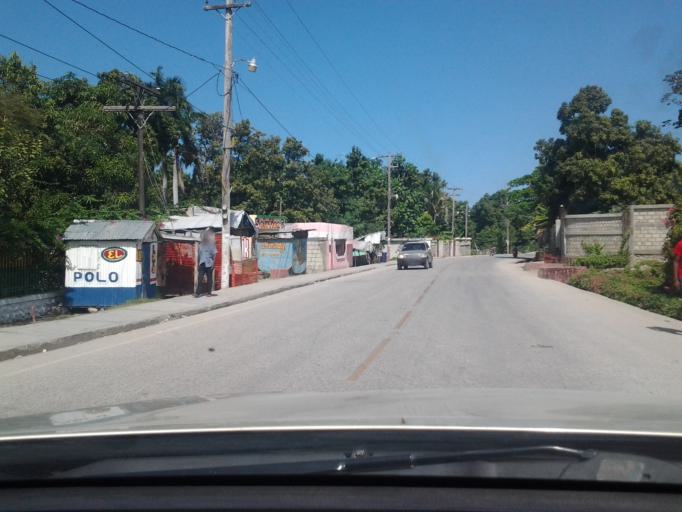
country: HT
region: Ouest
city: Tigwav
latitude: 18.4358
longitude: -72.8592
